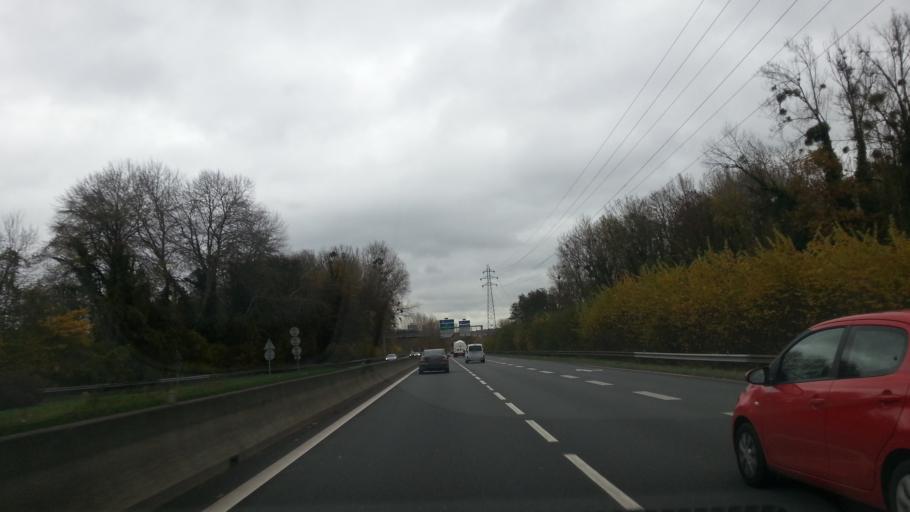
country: FR
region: Picardie
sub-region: Departement de l'Oise
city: Monchy-Saint-Eloi
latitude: 49.2858
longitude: 2.4713
